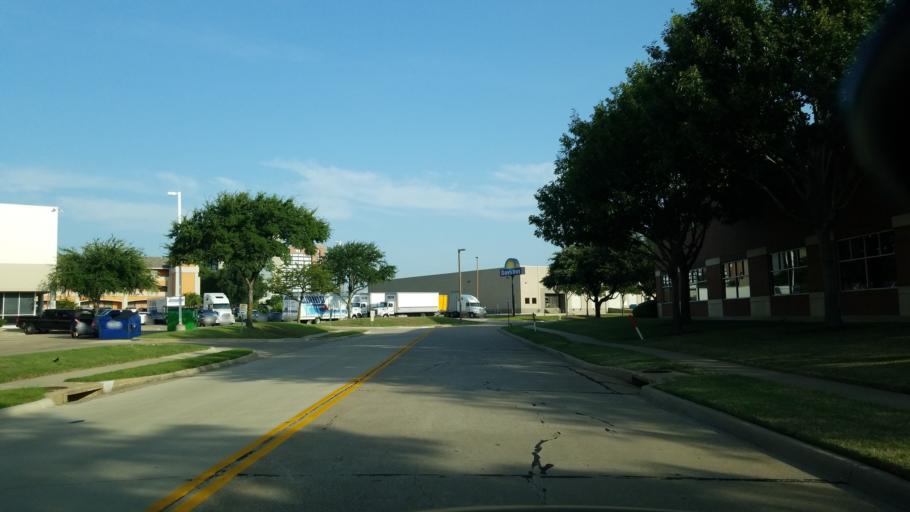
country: US
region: Texas
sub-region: Dallas County
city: Coppell
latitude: 32.9157
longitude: -97.0043
